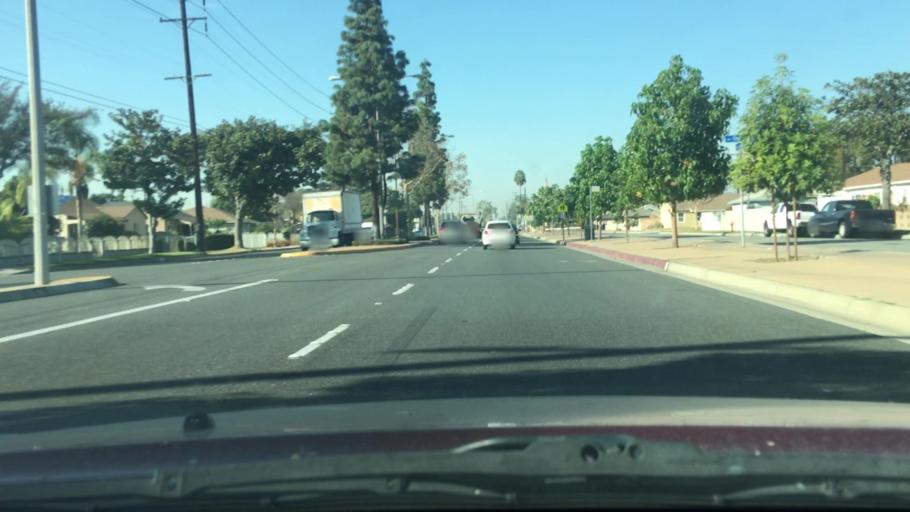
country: US
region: California
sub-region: Los Angeles County
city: Norwalk
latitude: 33.9022
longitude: -118.0955
